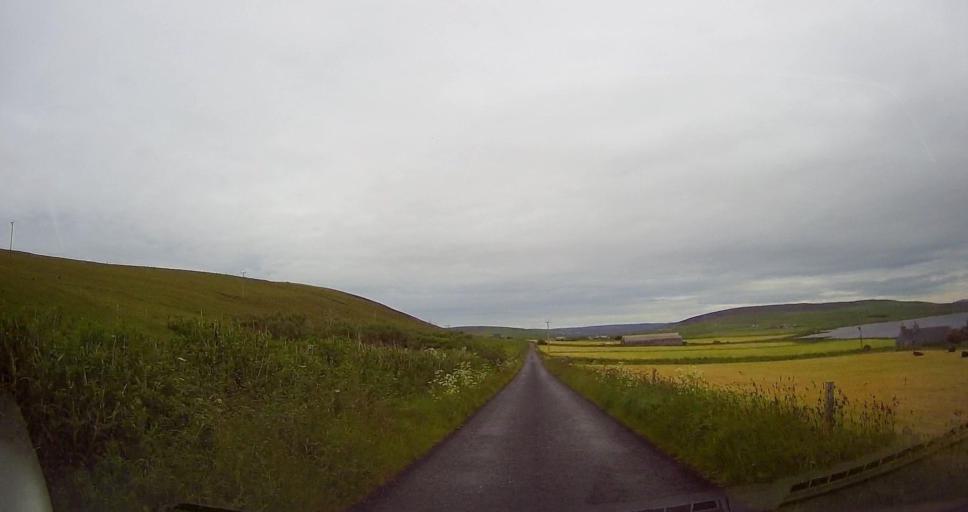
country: GB
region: Scotland
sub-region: Orkney Islands
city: Stromness
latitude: 59.1191
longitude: -3.2699
